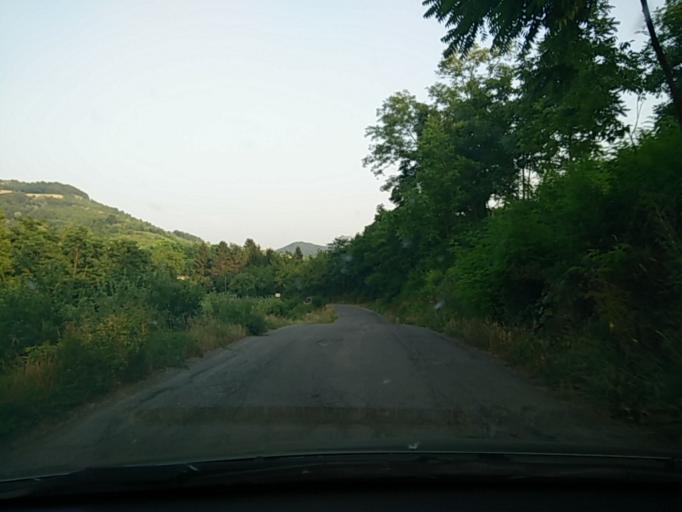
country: IT
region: Lombardy
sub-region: Provincia di Pavia
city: Susella
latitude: 44.9425
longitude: 9.1123
